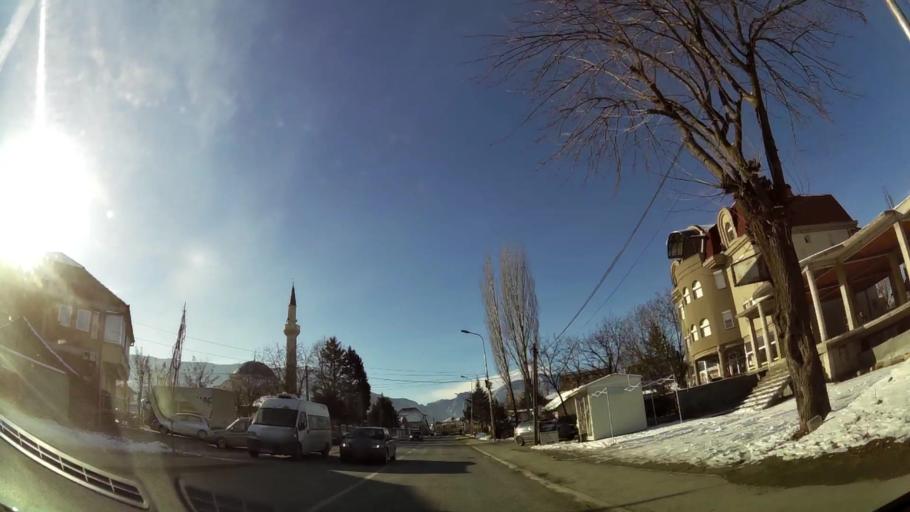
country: MK
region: Saraj
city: Saraj
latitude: 42.0025
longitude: 21.3311
